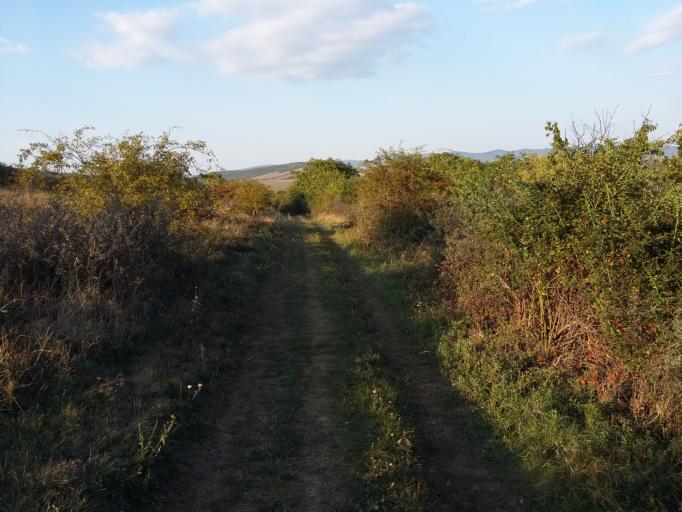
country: HU
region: Borsod-Abauj-Zemplen
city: Bekecs
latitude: 48.1569
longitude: 21.1723
